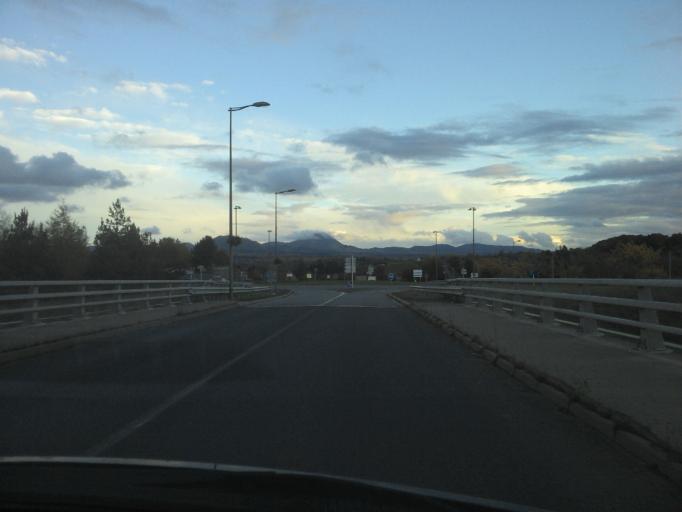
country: FR
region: Auvergne
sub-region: Departement du Puy-de-Dome
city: Chapdes-Beaufort
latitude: 45.8367
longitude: 2.8237
